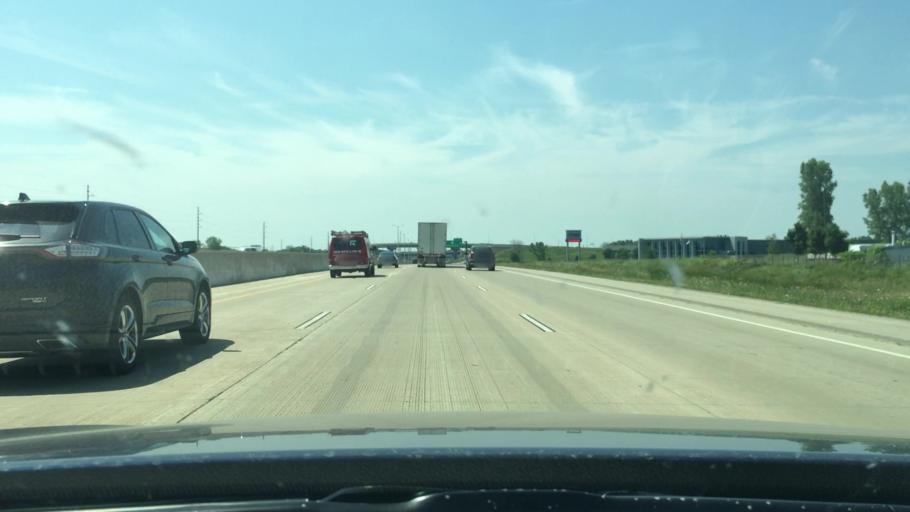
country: US
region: Wisconsin
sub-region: Winnebago County
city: Oshkosh
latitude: 44.0674
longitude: -88.5696
